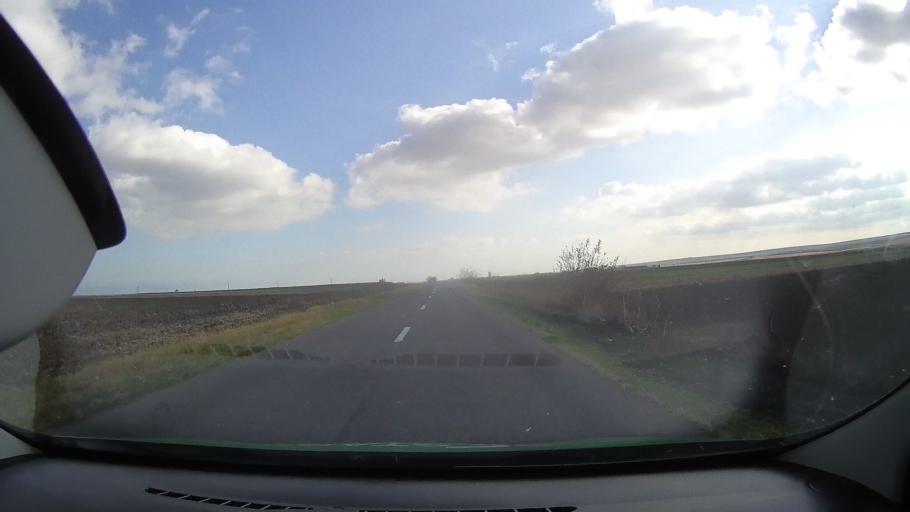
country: RO
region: Constanta
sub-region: Comuna Cogealac
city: Tariverde
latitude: 44.5538
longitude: 28.6215
